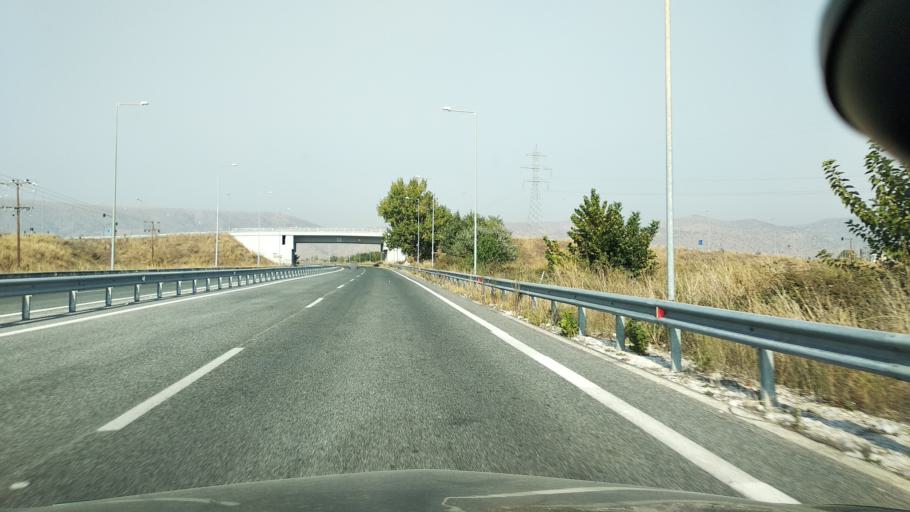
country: GR
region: Thessaly
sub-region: Trikala
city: Zarkos
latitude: 39.5926
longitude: 22.1256
